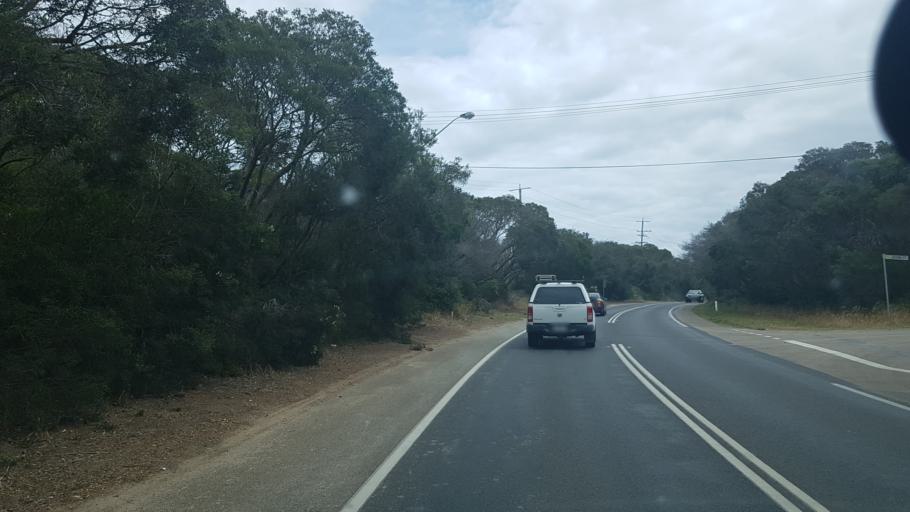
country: AU
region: Victoria
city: Rye
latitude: -38.3791
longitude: 144.8052
